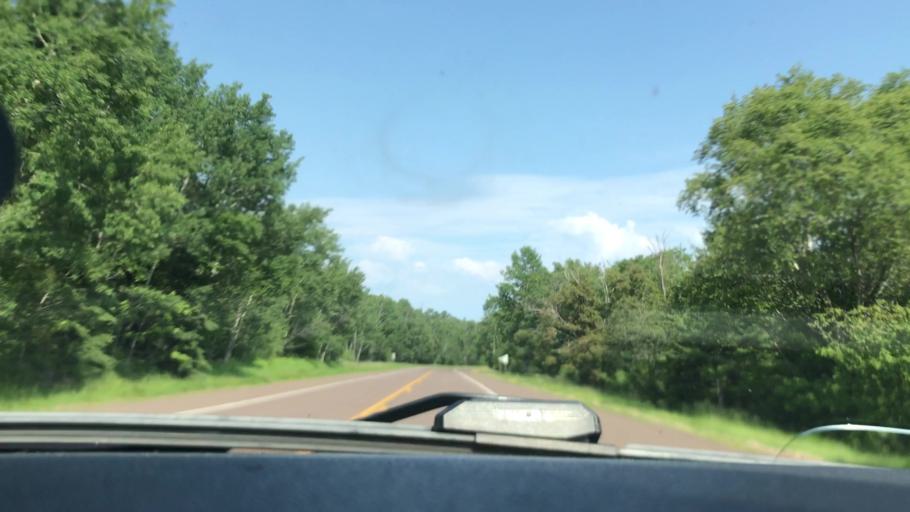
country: US
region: Minnesota
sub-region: Cook County
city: Grand Marais
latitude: 47.7774
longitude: -90.2206
